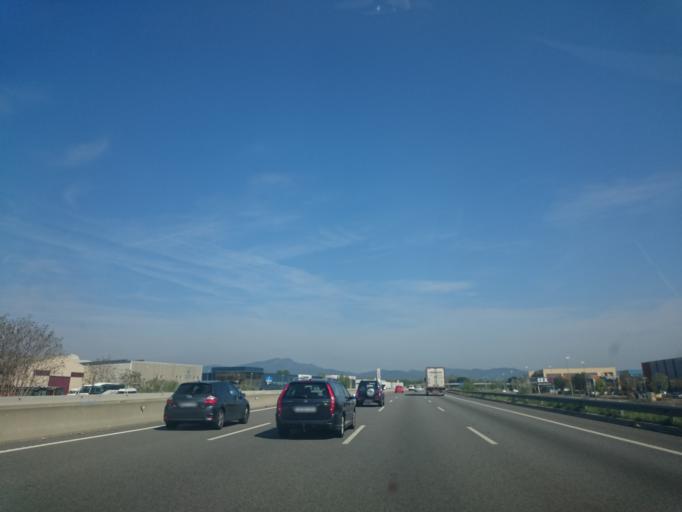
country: ES
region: Catalonia
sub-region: Provincia de Girona
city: Vilablareix
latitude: 41.9648
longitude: 2.7802
